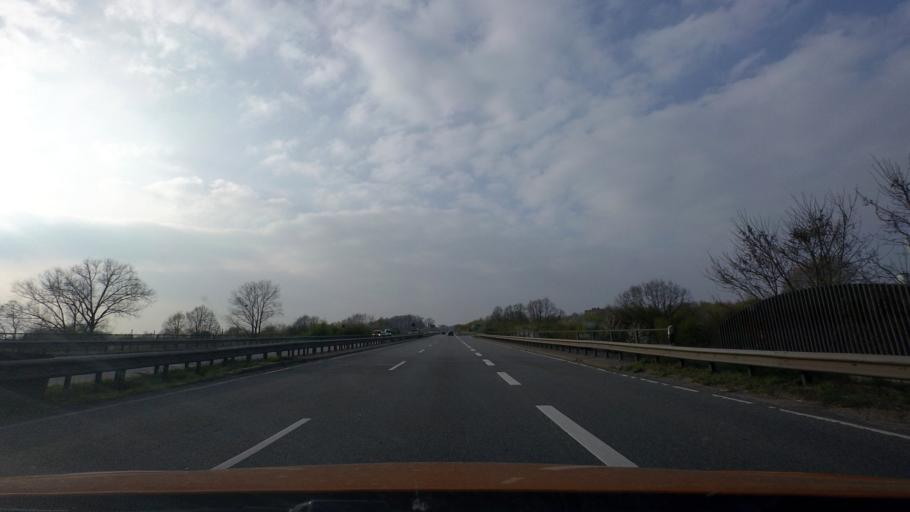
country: DE
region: North Rhine-Westphalia
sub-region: Regierungsbezirk Detmold
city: Herford
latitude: 52.1056
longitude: 8.6515
